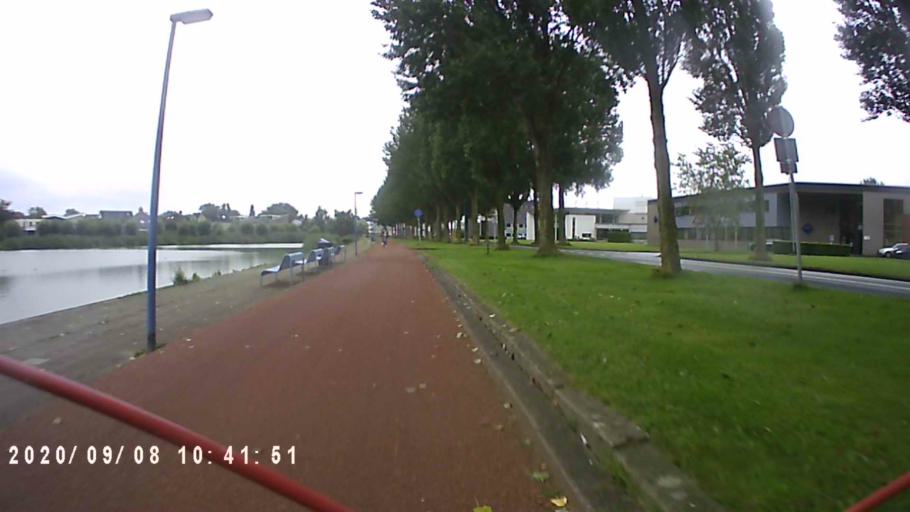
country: NL
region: Groningen
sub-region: Gemeente Groningen
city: Oosterpark
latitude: 53.2376
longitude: 6.6009
